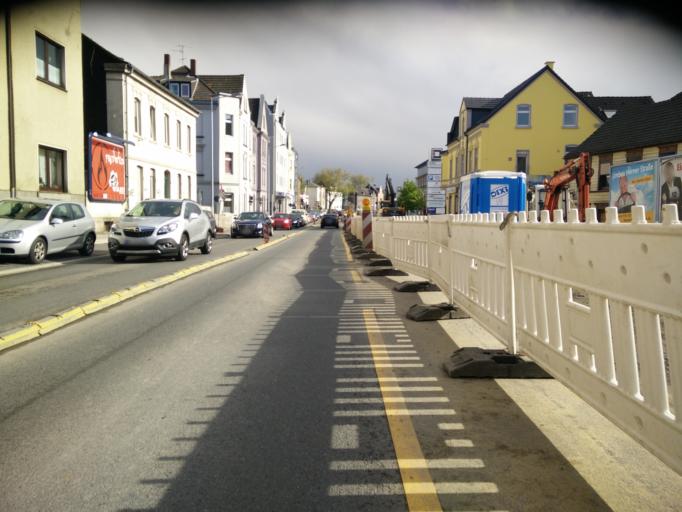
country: DE
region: North Rhine-Westphalia
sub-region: Regierungsbezirk Arnsberg
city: Bochum
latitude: 51.5067
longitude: 7.2121
